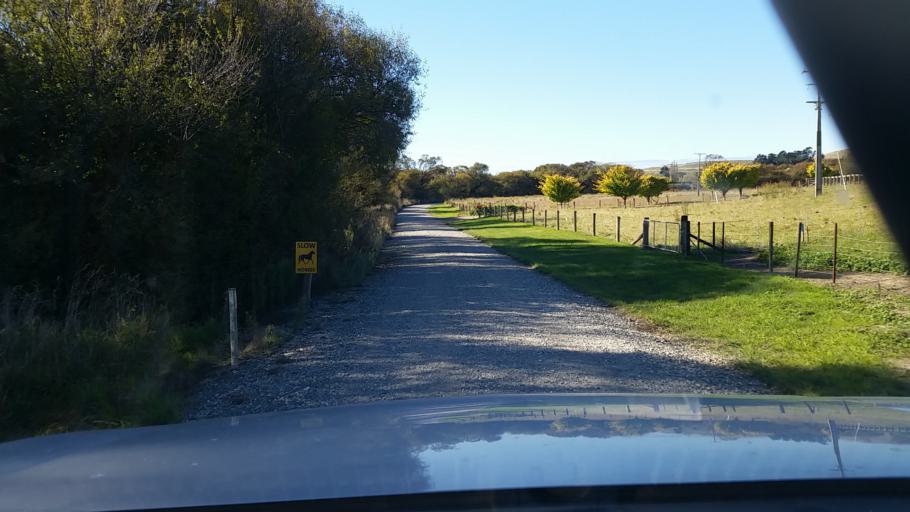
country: NZ
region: Marlborough
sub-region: Marlborough District
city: Blenheim
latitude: -41.6798
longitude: 174.1349
